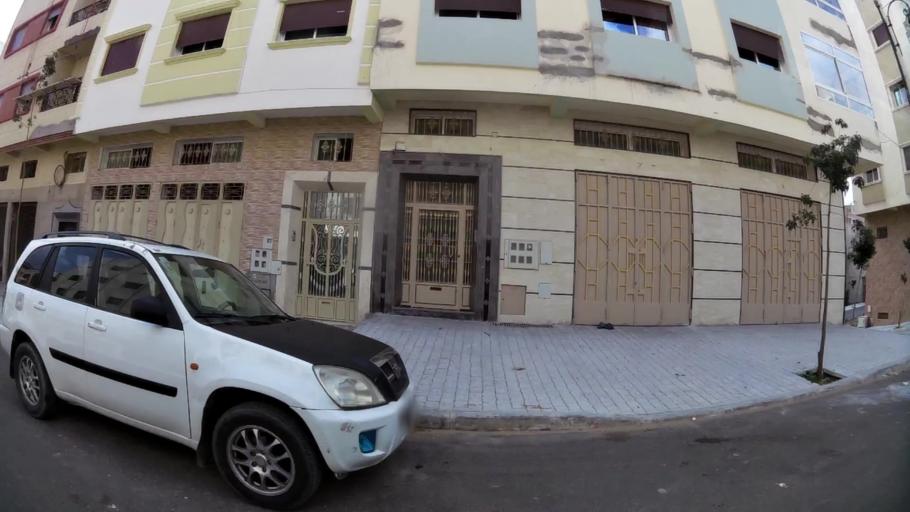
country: MA
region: Tanger-Tetouan
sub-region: Tanger-Assilah
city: Tangier
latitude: 35.7650
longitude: -5.7608
